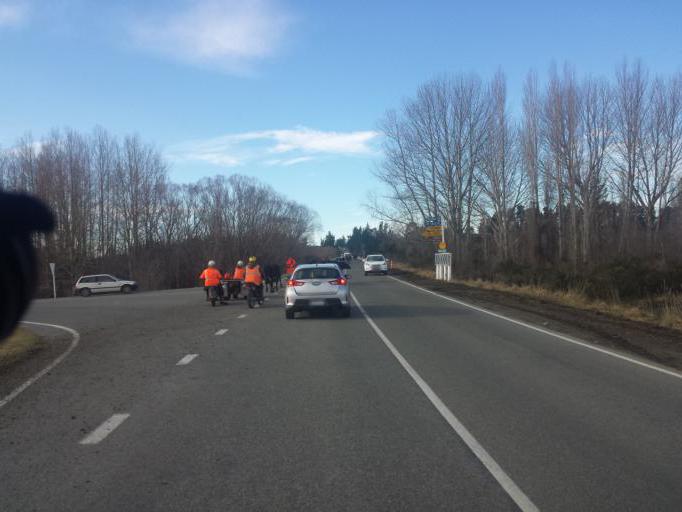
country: NZ
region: Canterbury
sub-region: Timaru District
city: Pleasant Point
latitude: -43.9753
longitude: 171.2976
